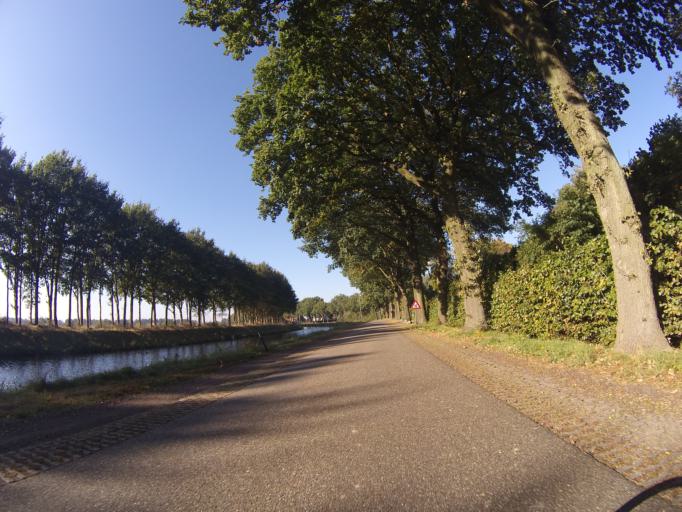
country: NL
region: Drenthe
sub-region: Gemeente Coevorden
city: Dalen
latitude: 52.7428
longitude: 6.7590
